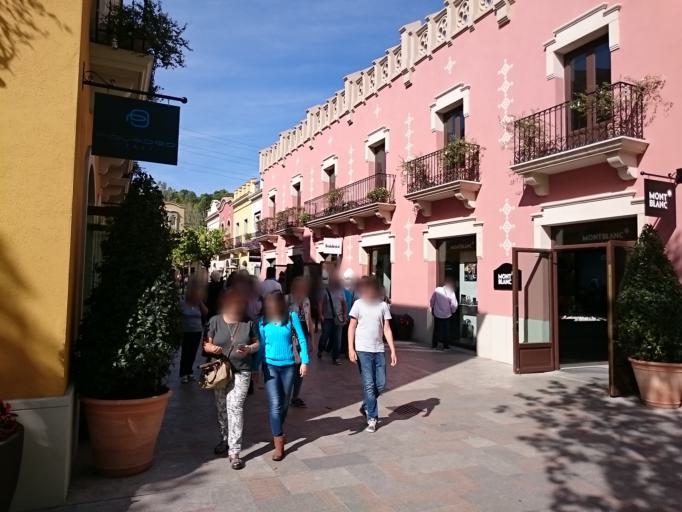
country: ES
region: Catalonia
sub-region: Provincia de Barcelona
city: Cardedeu
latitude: 41.6123
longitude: 2.3451
